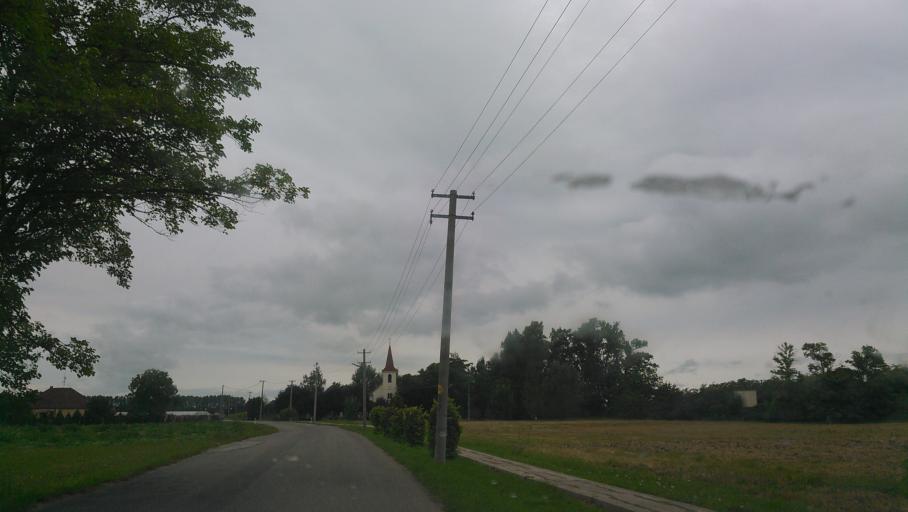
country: SK
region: Nitriansky
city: Kolarovo
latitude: 47.8903
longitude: 17.8959
